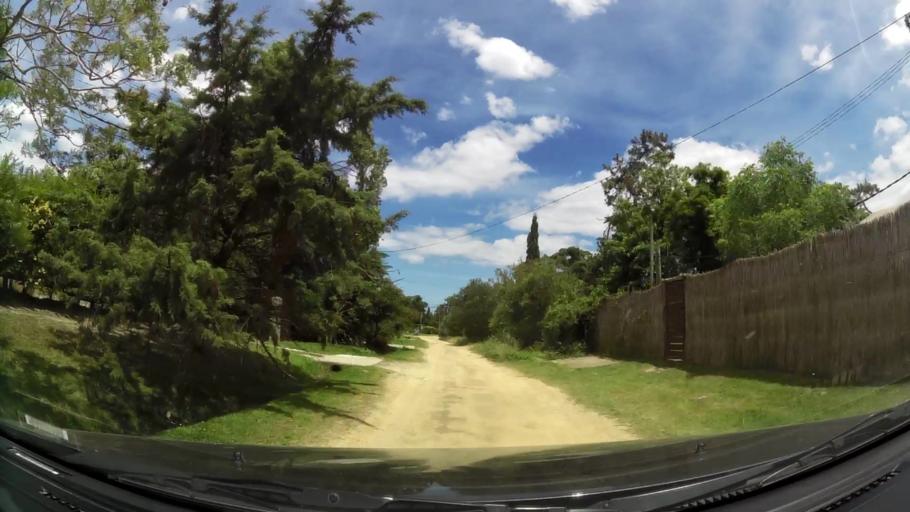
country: UY
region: Canelones
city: Pando
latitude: -34.8040
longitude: -55.8993
